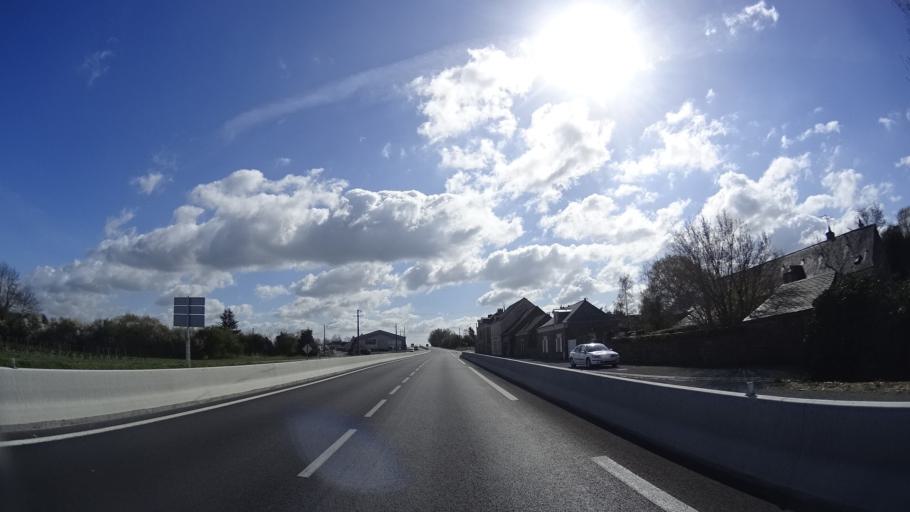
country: FR
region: Pays de la Loire
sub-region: Departement de Maine-et-Loire
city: Saint-Melaine-sur-Aubance
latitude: 47.3884
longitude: -0.4956
